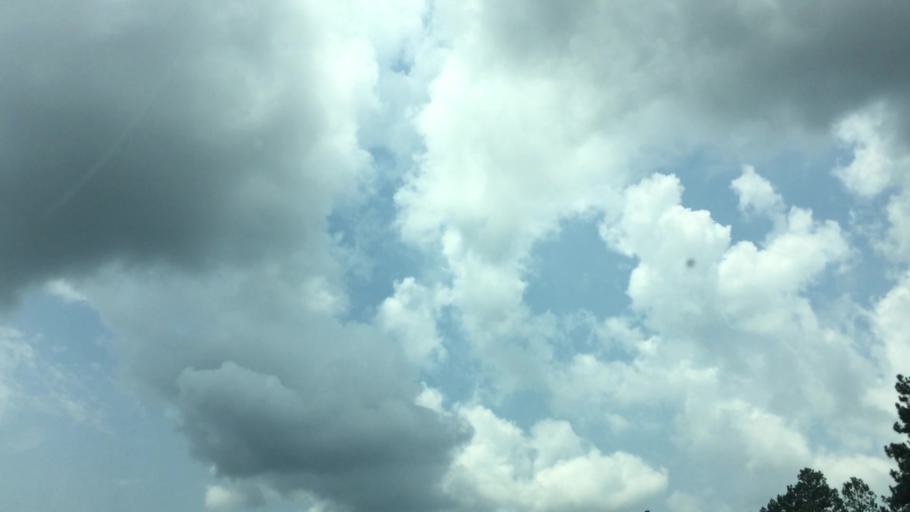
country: US
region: Georgia
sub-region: Fulton County
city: Palmetto
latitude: 33.5801
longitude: -84.6666
